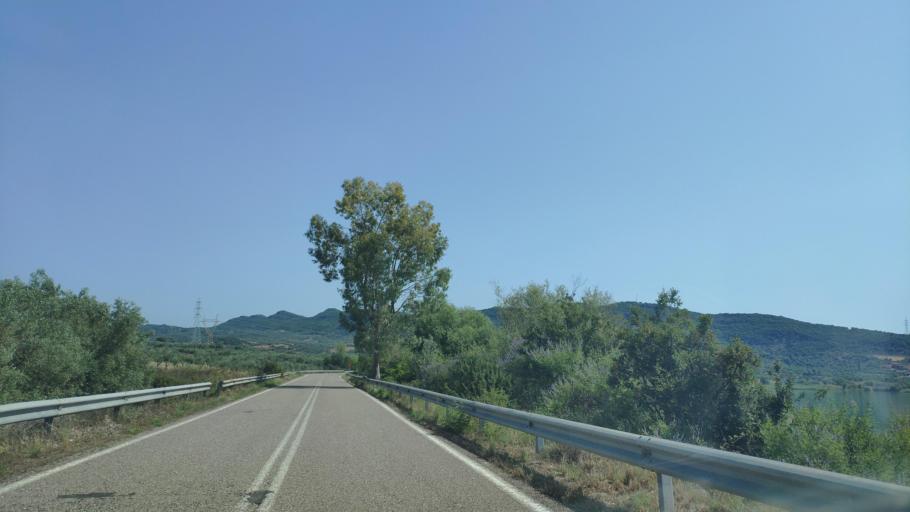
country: GR
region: West Greece
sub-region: Nomos Aitolias kai Akarnanias
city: Lepenou
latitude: 38.7015
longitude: 21.3215
